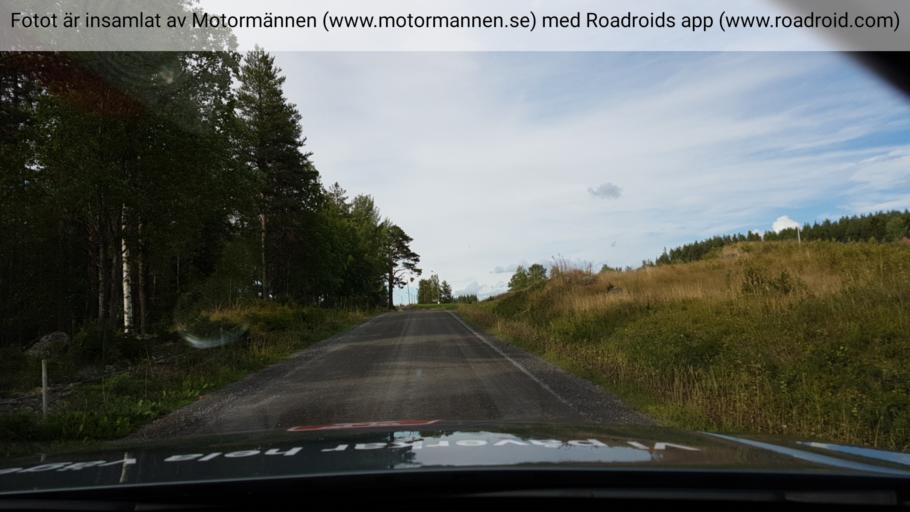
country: SE
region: Jaemtland
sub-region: Braecke Kommun
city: Braecke
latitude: 63.2790
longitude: 15.3707
